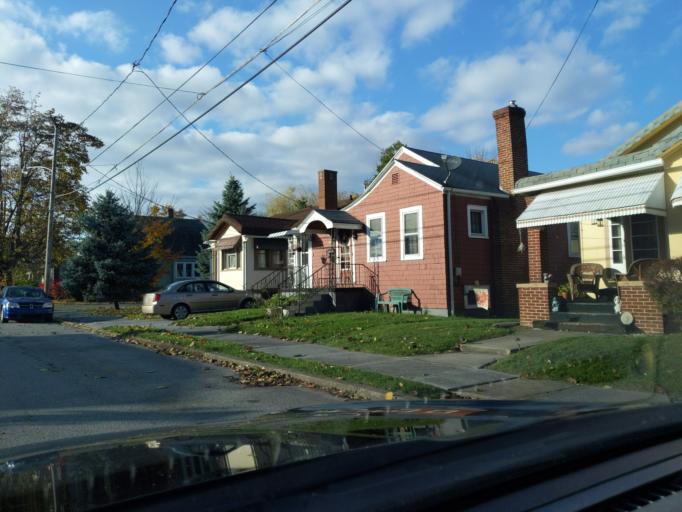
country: US
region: Pennsylvania
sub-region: Blair County
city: Lakemont
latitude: 40.4781
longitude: -78.4014
